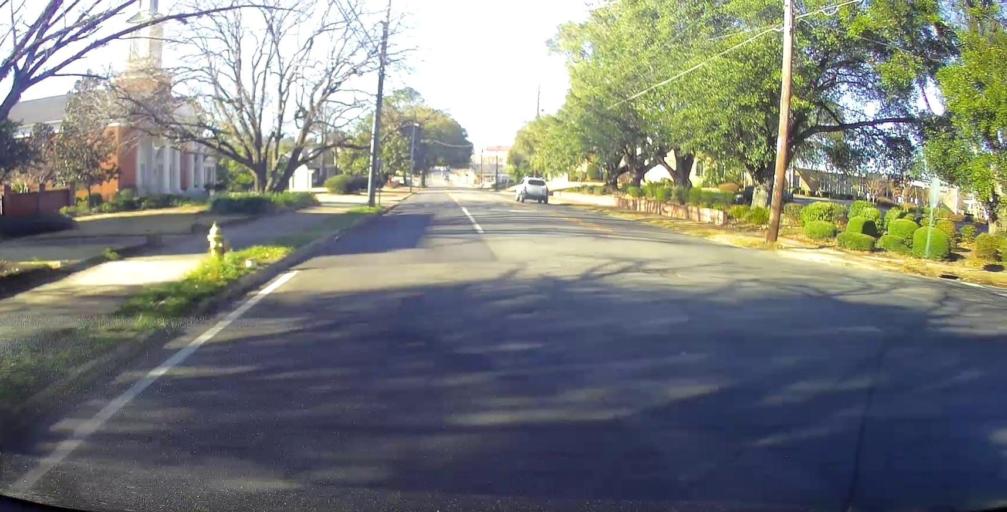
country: US
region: Georgia
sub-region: Sumter County
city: Americus
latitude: 32.0687
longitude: -84.2313
